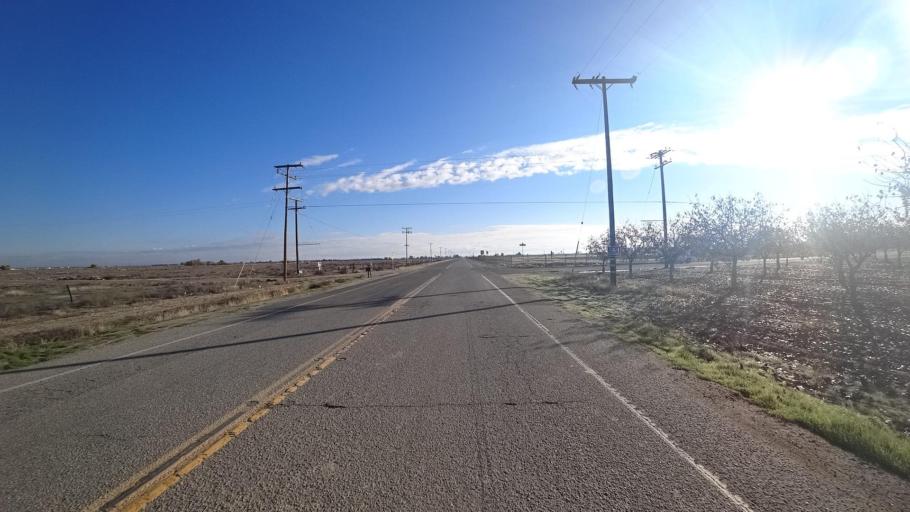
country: US
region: California
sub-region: Kern County
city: Delano
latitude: 35.7758
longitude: -119.3304
